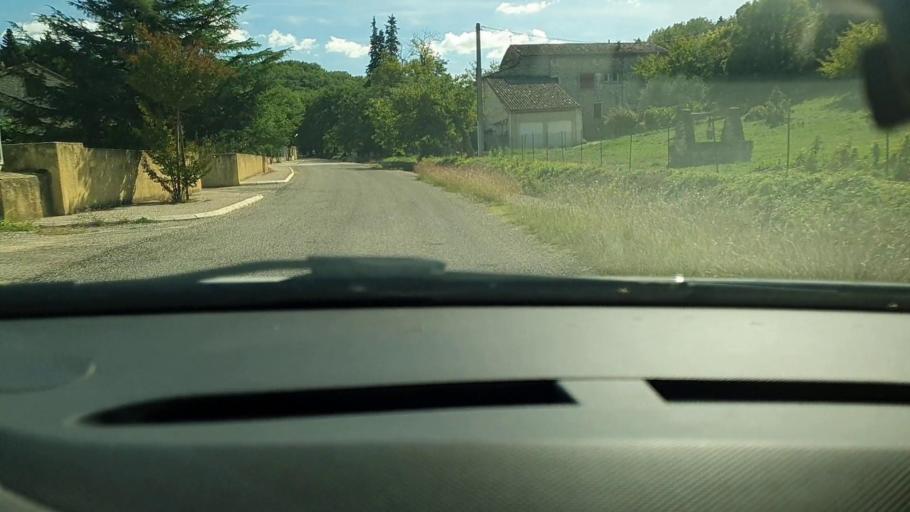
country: FR
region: Languedoc-Roussillon
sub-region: Departement du Gard
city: Saint-Ambroix
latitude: 44.2292
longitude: 4.2819
